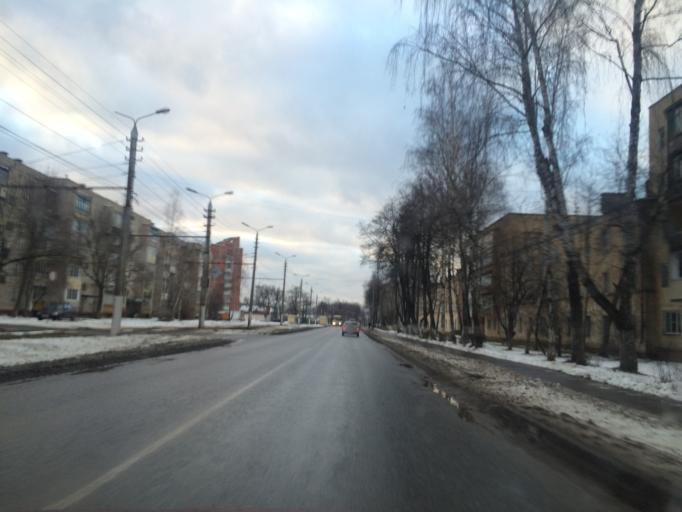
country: RU
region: Tula
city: Tula
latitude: 54.2195
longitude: 37.7007
